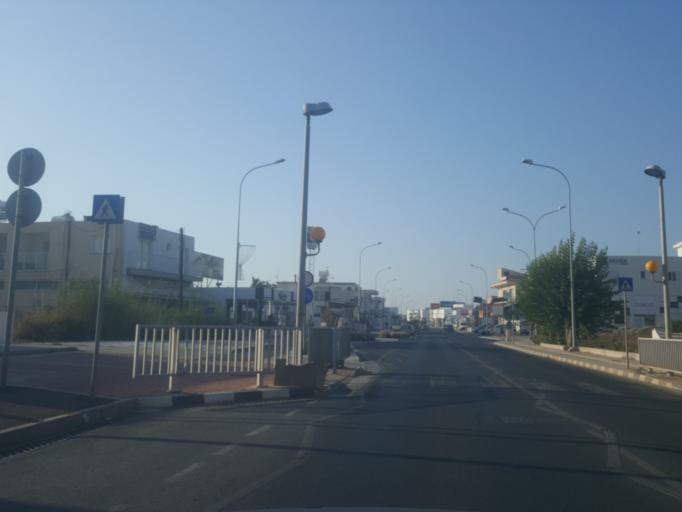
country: CY
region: Ammochostos
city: Paralimni
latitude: 35.0455
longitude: 33.9777
